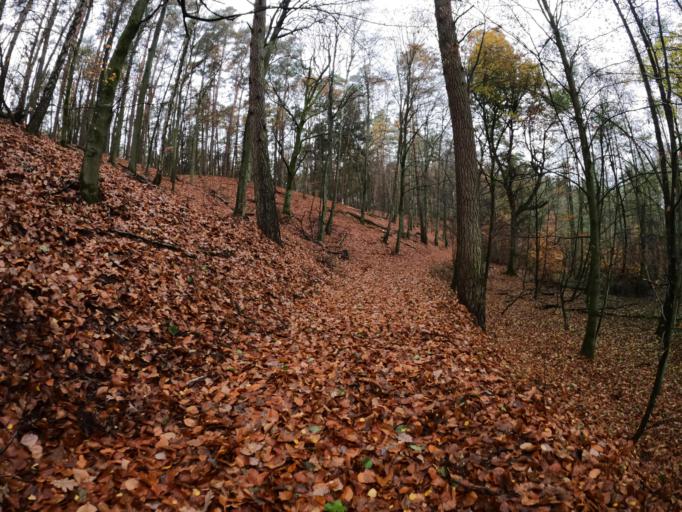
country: PL
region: West Pomeranian Voivodeship
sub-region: Powiat walecki
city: Tuczno
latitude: 53.2700
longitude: 16.2521
